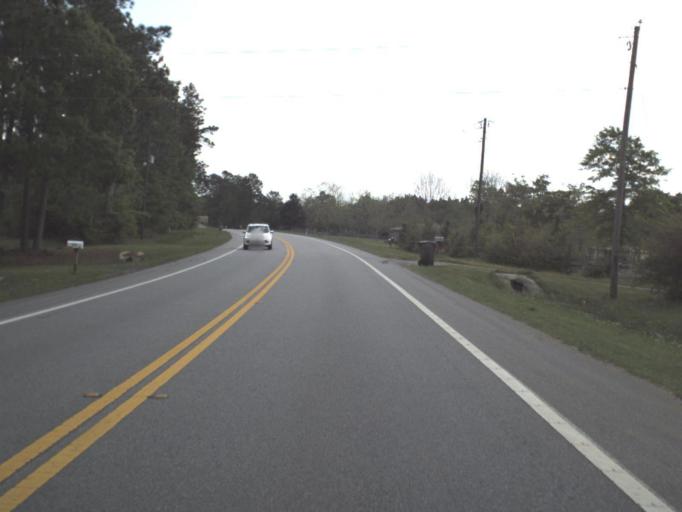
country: US
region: Florida
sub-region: Escambia County
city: Molino
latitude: 30.7970
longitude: -87.4219
